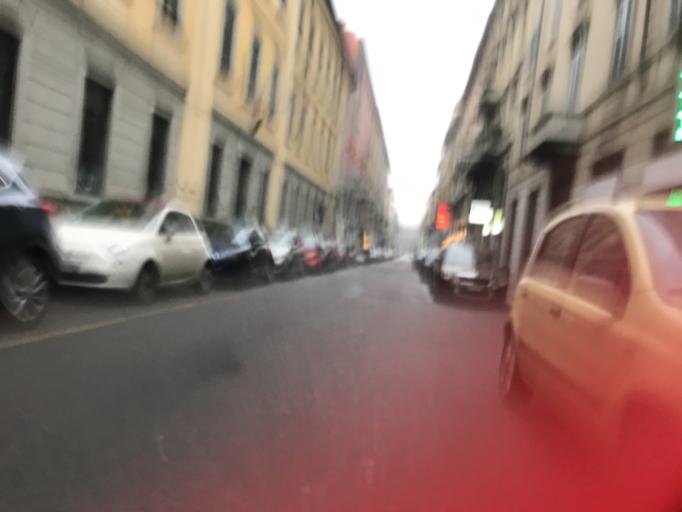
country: IT
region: Lombardy
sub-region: Citta metropolitana di Milano
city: Milano
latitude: 45.4796
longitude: 9.1887
